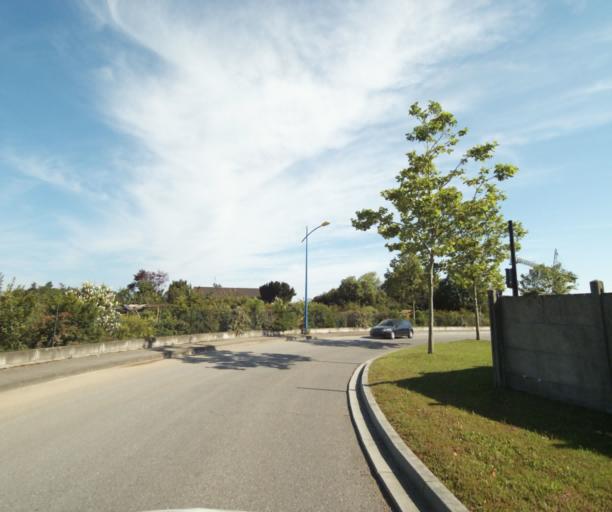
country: FR
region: Rhone-Alpes
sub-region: Departement de la Haute-Savoie
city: Marin
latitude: 46.3960
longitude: 6.5061
